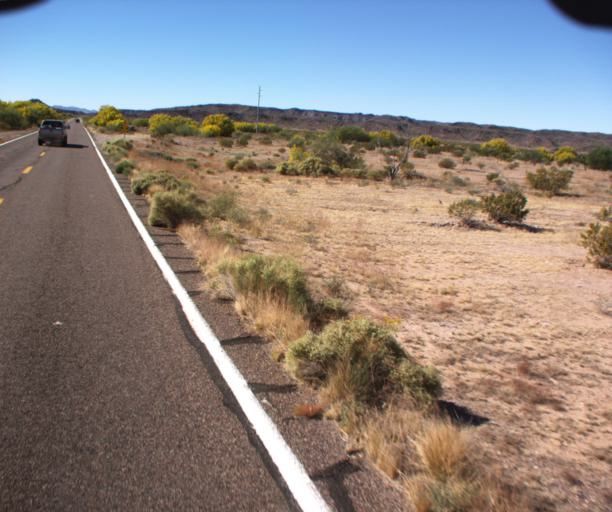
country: US
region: Arizona
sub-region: Pima County
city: Ajo
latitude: 32.5838
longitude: -112.8733
